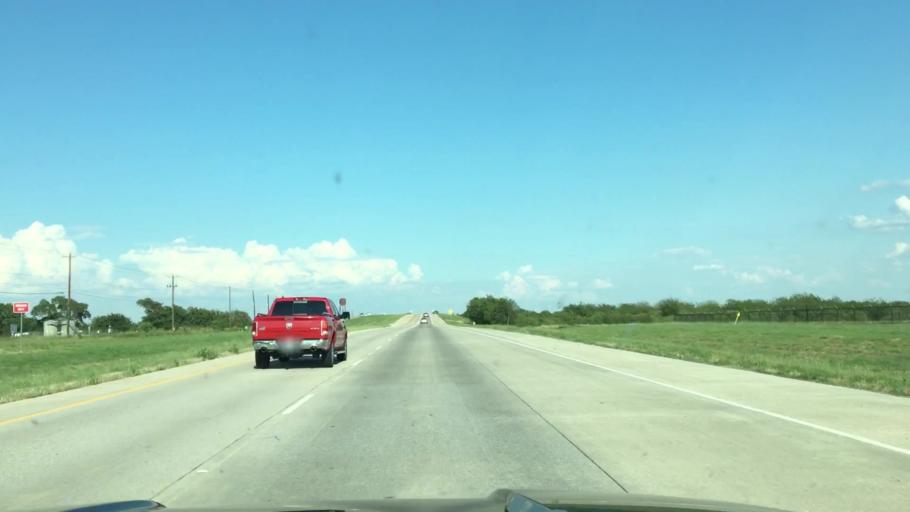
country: US
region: Texas
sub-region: Tarrant County
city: Haslet
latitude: 33.0353
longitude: -97.3477
